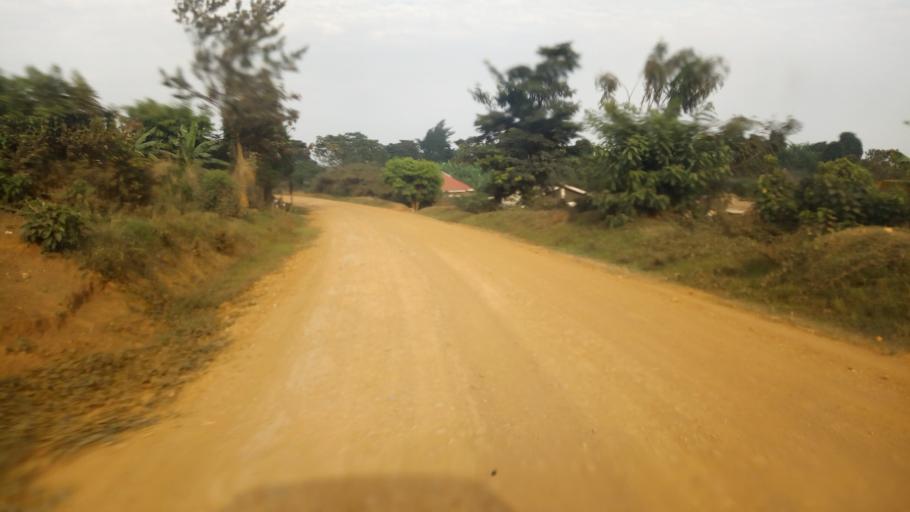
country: UG
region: Western Region
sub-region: Kanungu District
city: Ntungamo
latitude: -0.8279
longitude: 29.7007
